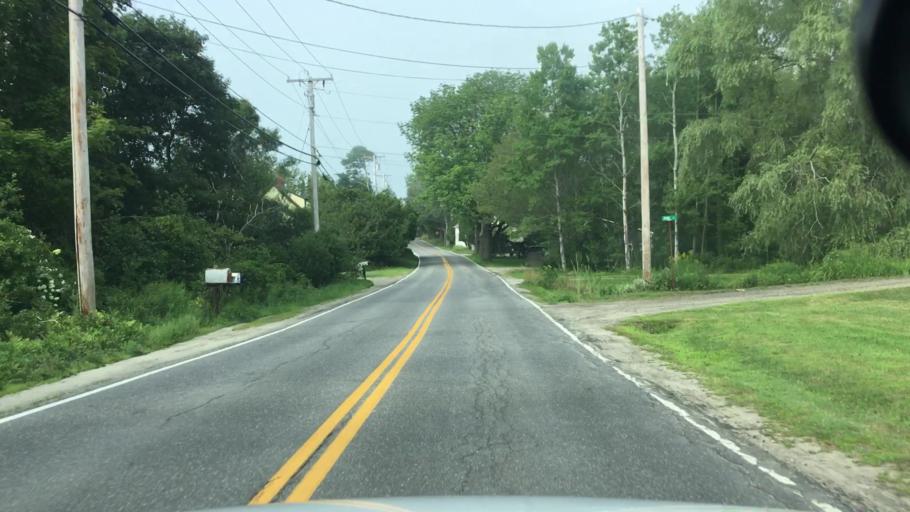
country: US
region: Maine
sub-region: Cumberland County
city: Harpswell Center
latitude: 43.7621
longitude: -69.9759
